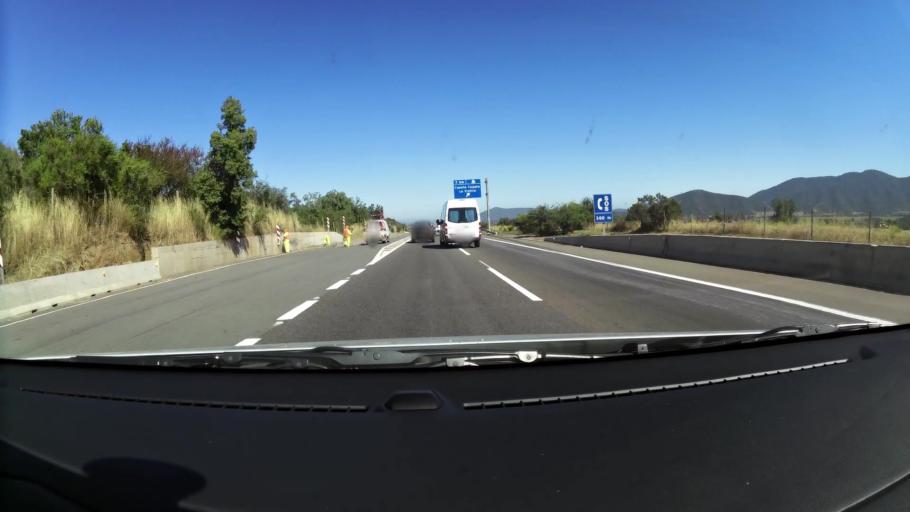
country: CL
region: Santiago Metropolitan
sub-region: Provincia de Melipilla
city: Melipilla
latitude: -33.3776
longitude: -71.2840
